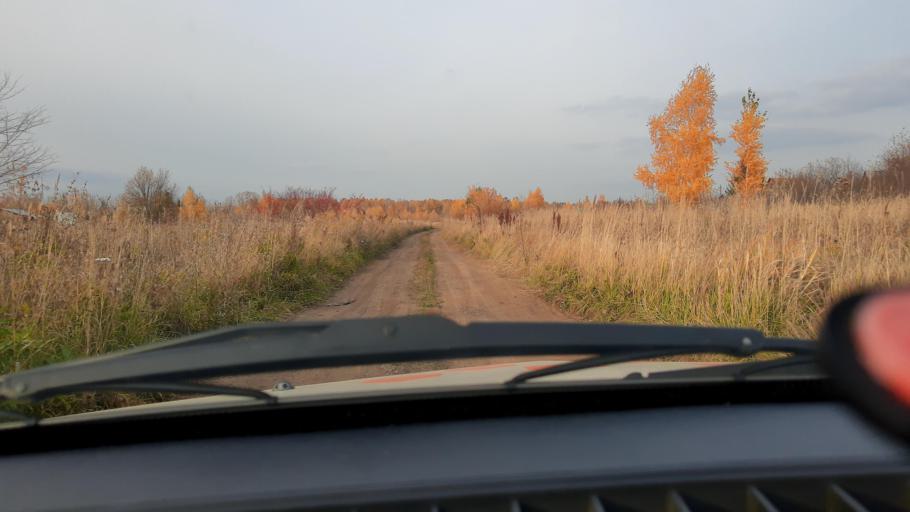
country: RU
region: Bashkortostan
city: Iglino
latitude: 54.8014
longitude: 56.3468
